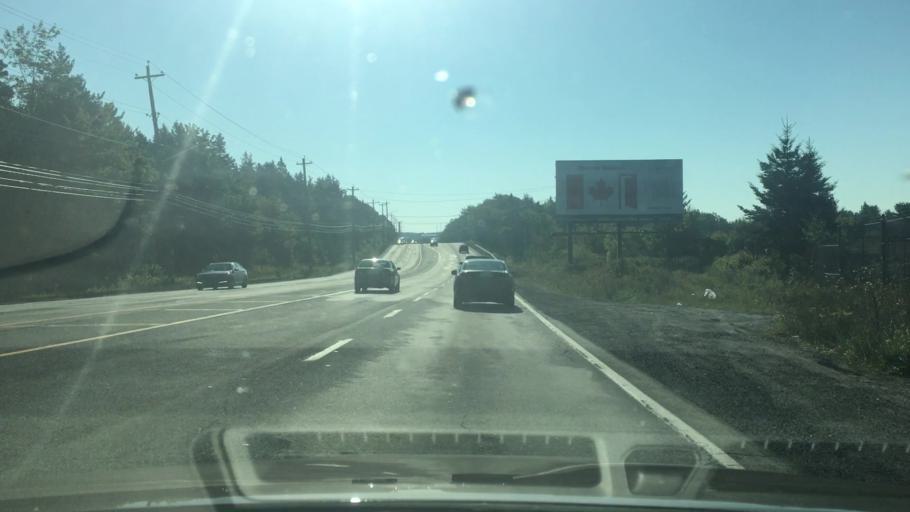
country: CA
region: Nova Scotia
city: Dartmouth
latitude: 44.7062
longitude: -63.6190
